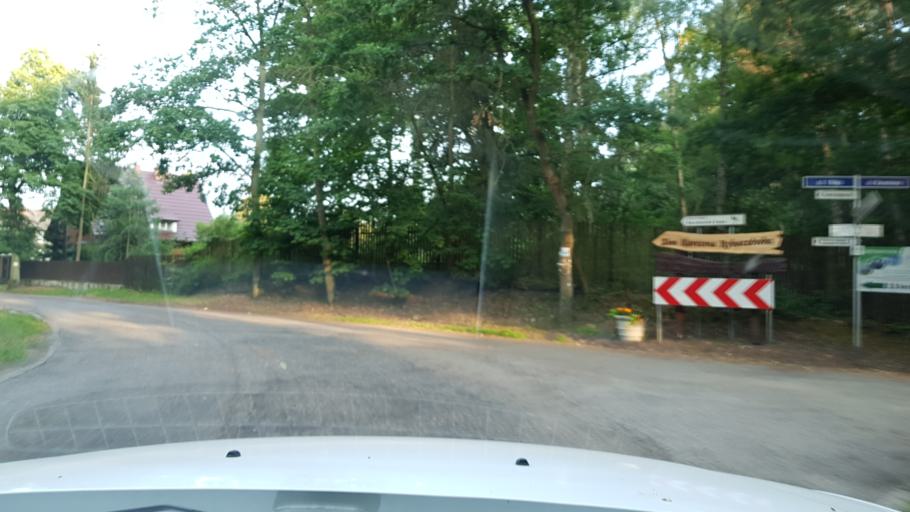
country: PL
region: West Pomeranian Voivodeship
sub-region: Swinoujscie
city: Swinoujscie
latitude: 53.8524
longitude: 14.2861
